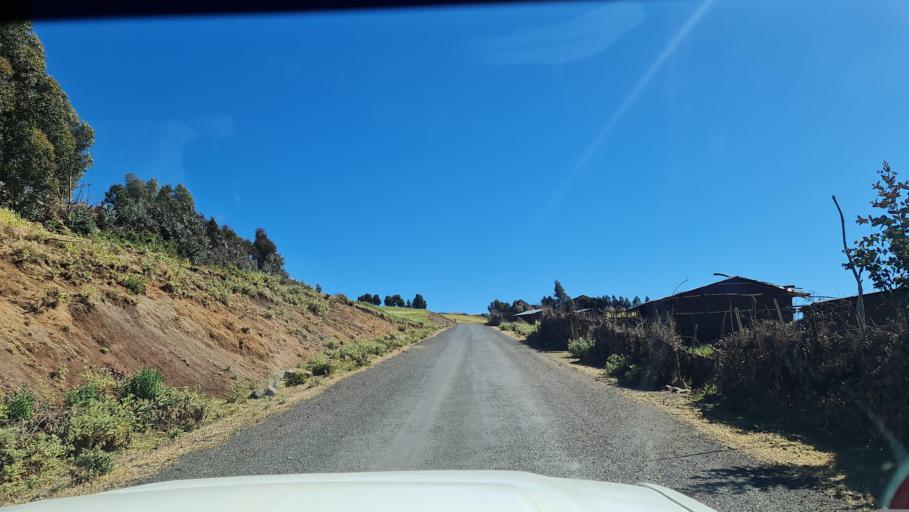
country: ET
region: Amhara
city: Debark'
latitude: 13.1331
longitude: 38.1701
